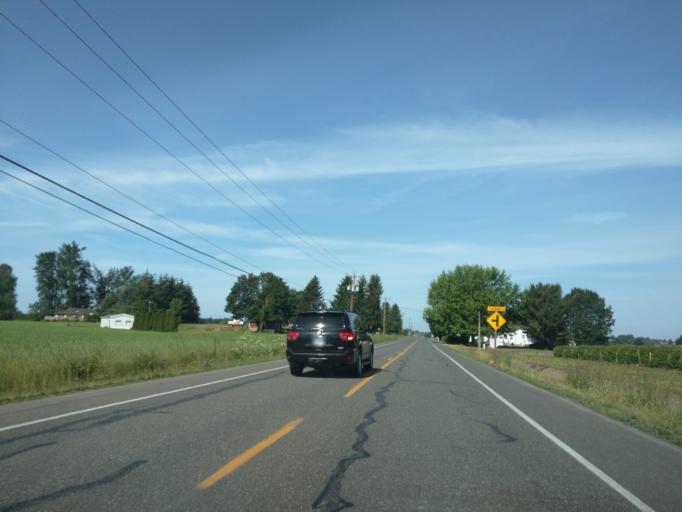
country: US
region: Washington
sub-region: Whatcom County
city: Everson
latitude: 48.9420
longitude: -122.3892
